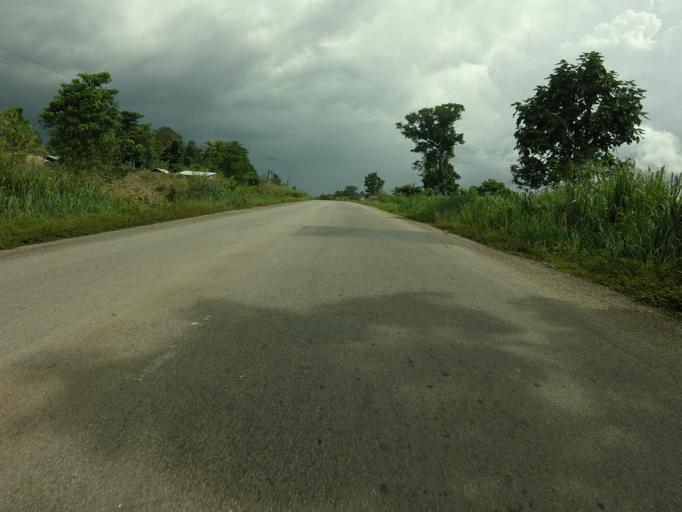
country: TG
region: Plateaux
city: Badou
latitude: 7.7064
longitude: 0.5303
